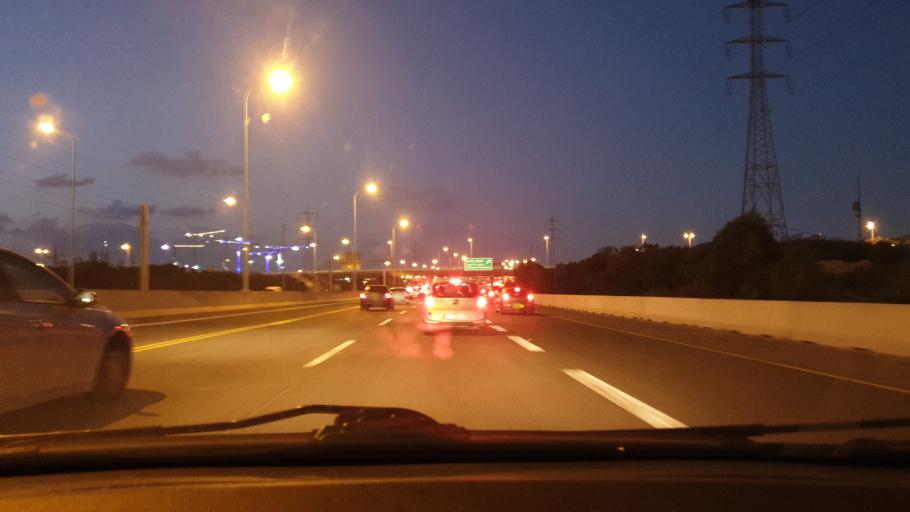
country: IL
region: Central District
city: Rishon LeZiyyon
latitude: 31.9775
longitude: 34.7560
